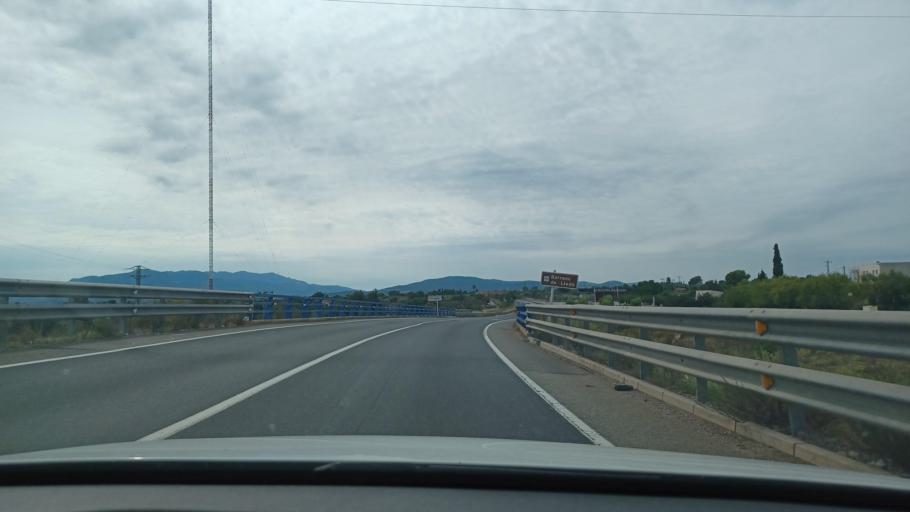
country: ES
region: Catalonia
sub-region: Provincia de Tarragona
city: Santa Barbara
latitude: 40.7397
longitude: 0.5045
